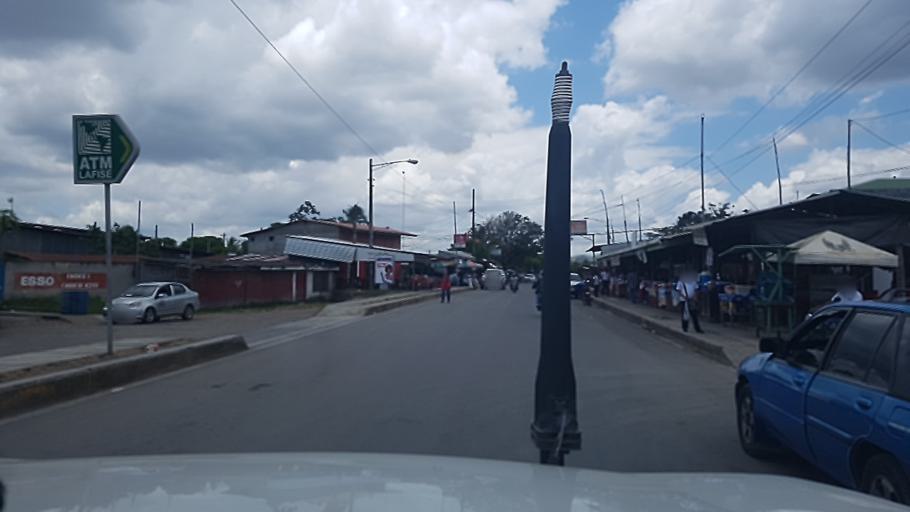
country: NI
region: Chontales
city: Santo Tomas
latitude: 12.0674
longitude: -85.0925
